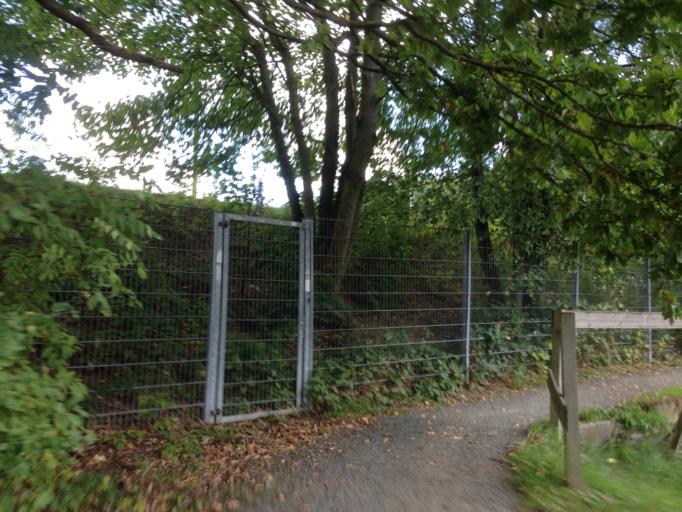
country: DE
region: Hesse
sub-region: Regierungsbezirk Giessen
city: Giessen
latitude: 50.5850
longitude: 8.7045
